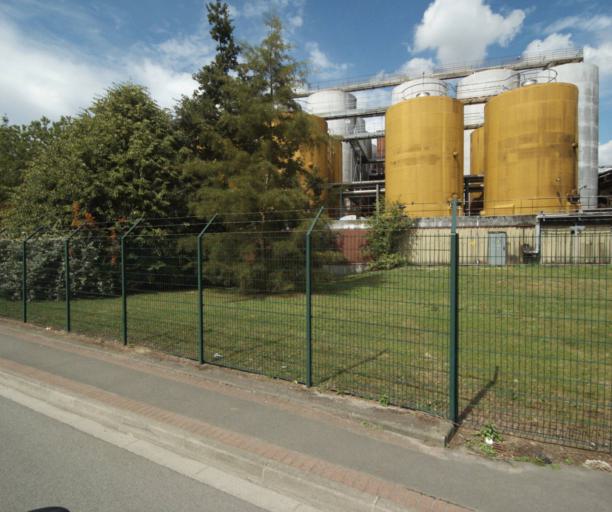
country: FR
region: Nord-Pas-de-Calais
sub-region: Departement du Nord
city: Mons-en-Baroeul
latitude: 50.6476
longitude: 3.1135
